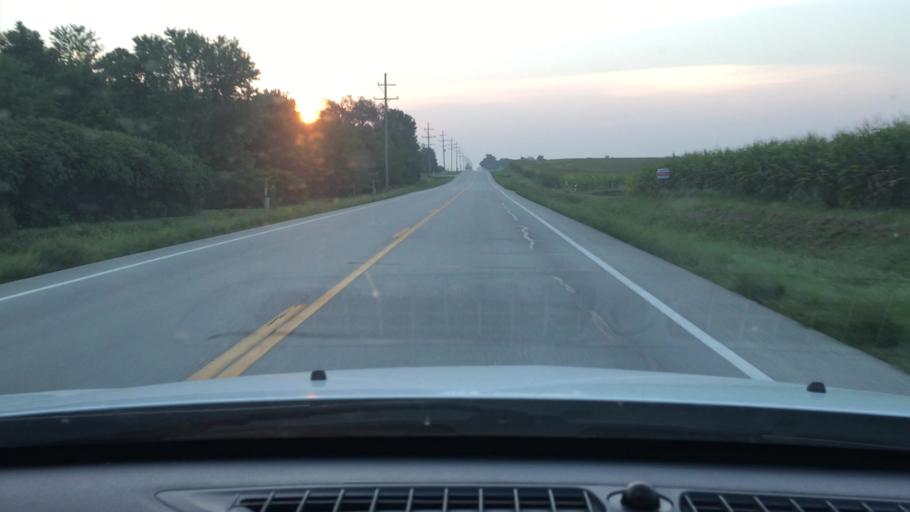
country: US
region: Illinois
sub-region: DeKalb County
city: Waterman
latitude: 41.8491
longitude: -88.7900
